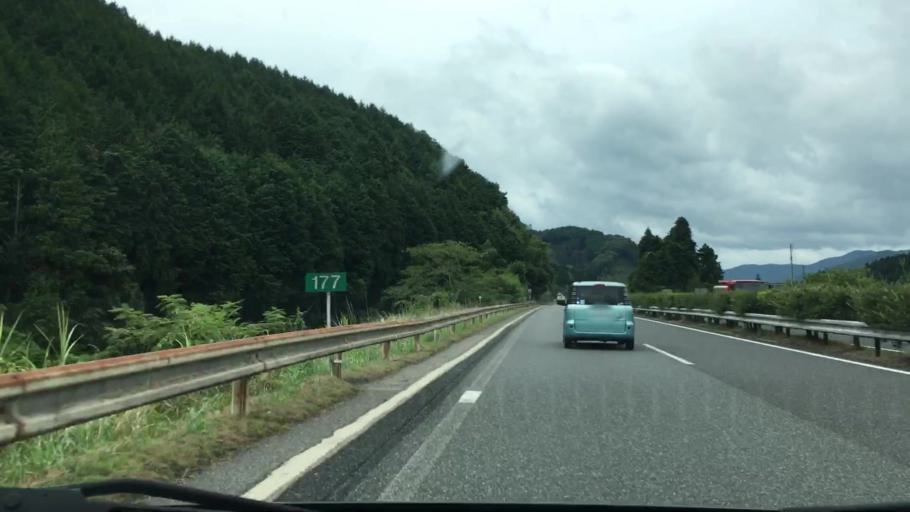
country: JP
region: Okayama
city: Tsuyama
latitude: 35.0387
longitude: 133.7934
